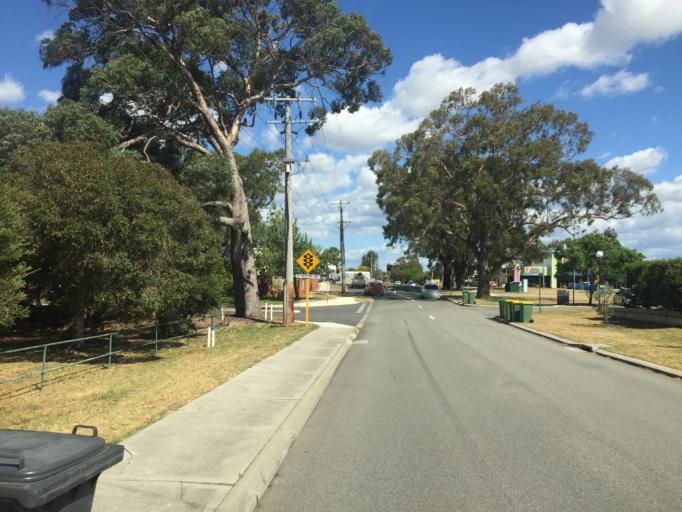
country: AU
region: Western Australia
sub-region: Belmont
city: Redcliffe
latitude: -31.9281
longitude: 115.9456
